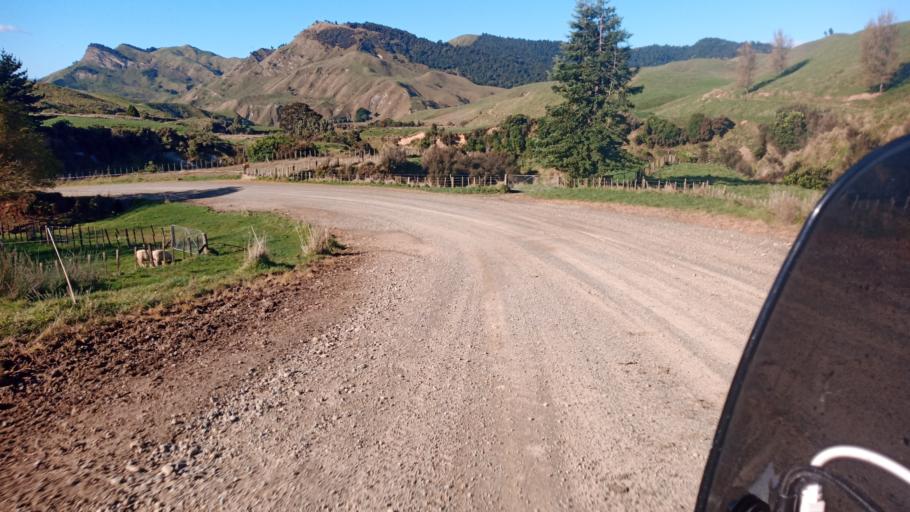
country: NZ
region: Hawke's Bay
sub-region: Wairoa District
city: Wairoa
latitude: -38.7404
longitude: 177.2900
